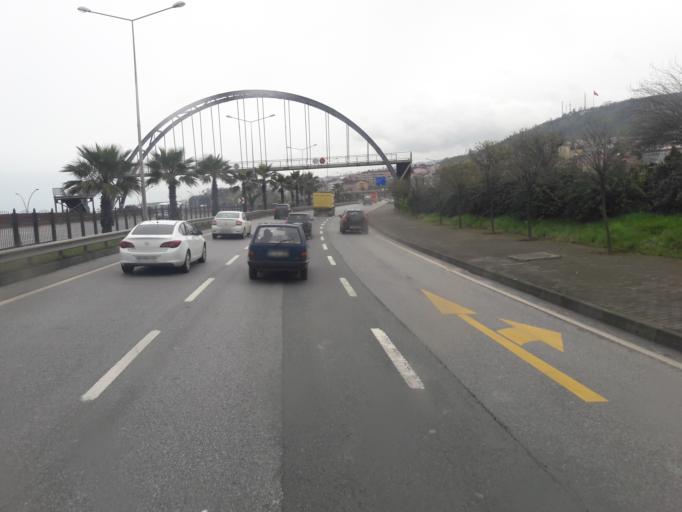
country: TR
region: Trabzon
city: Trabzon
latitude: 41.0118
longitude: 39.7225
